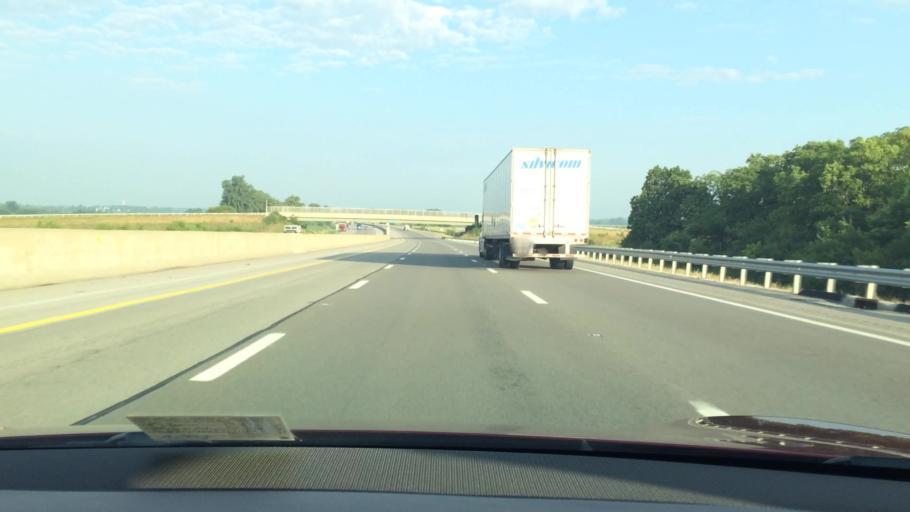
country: US
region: Ohio
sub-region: Huron County
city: Bellevue
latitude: 41.3461
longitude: -82.7907
